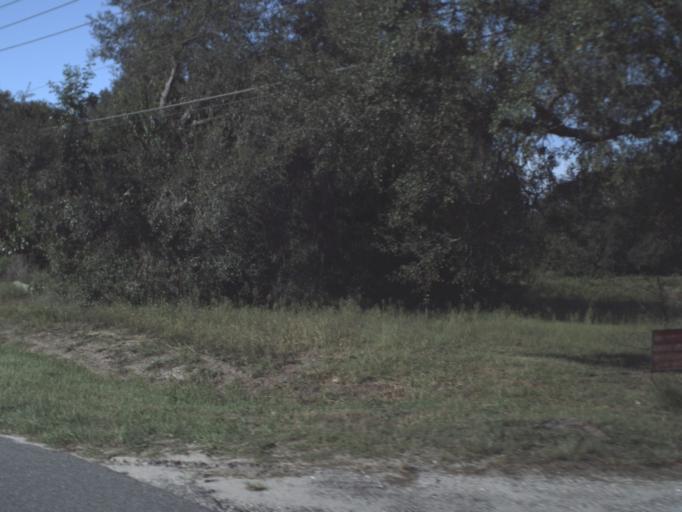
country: US
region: Florida
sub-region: Polk County
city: Davenport
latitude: 28.1773
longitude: -81.5952
